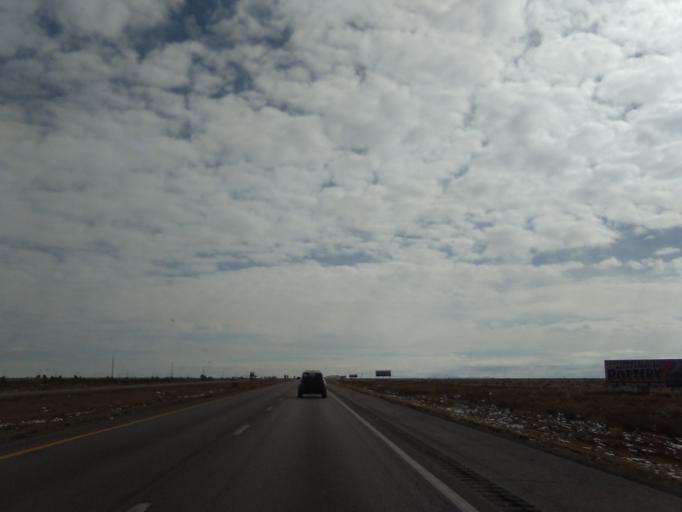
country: US
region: New Mexico
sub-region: Hidalgo County
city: Lordsburg
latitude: 32.2413
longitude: -108.4885
